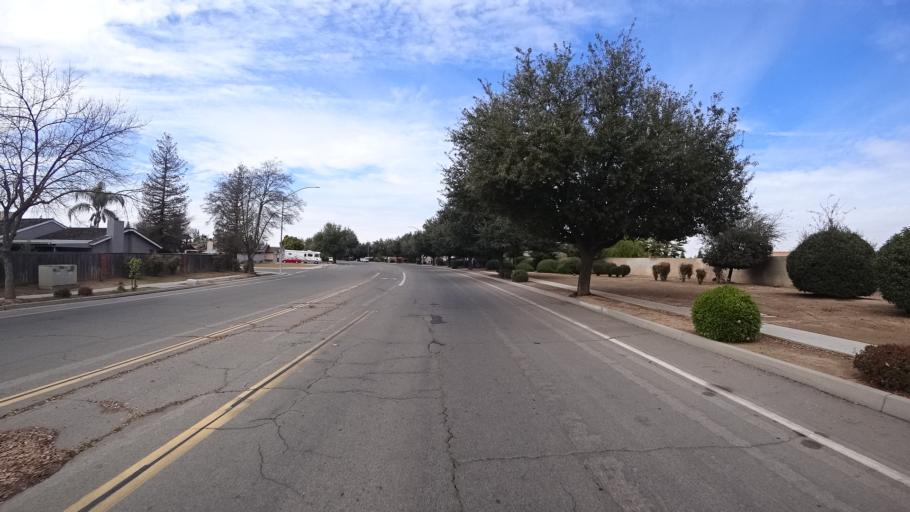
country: US
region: California
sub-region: Fresno County
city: West Park
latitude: 36.8333
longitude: -119.8806
